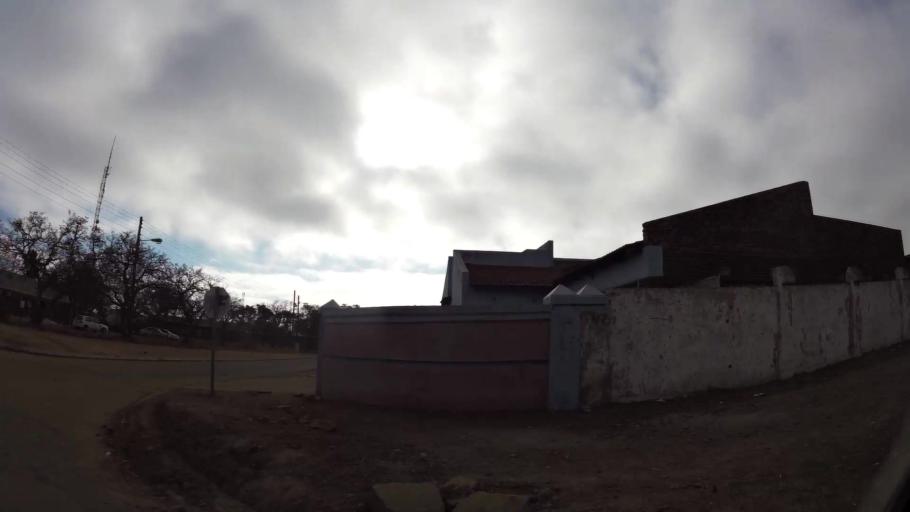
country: ZA
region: Limpopo
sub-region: Capricorn District Municipality
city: Polokwane
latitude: -23.8425
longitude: 29.3864
